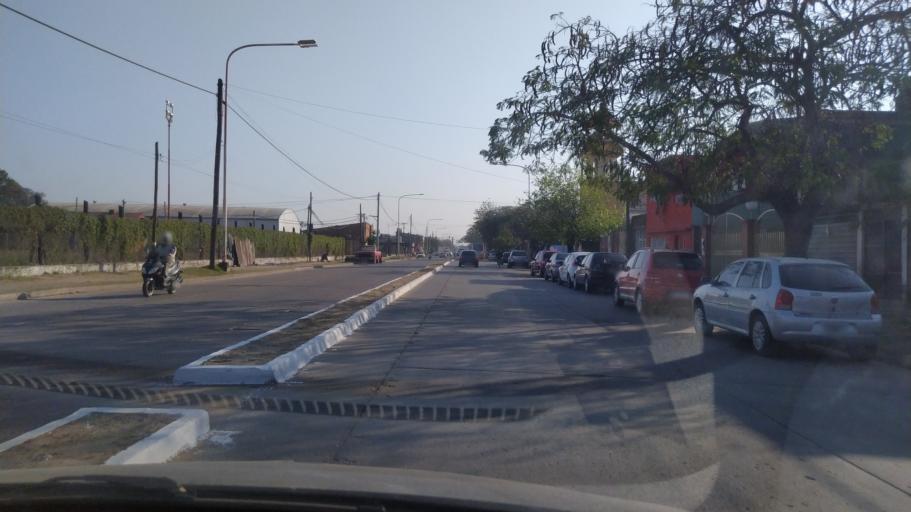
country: AR
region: Corrientes
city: Corrientes
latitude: -27.4850
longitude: -58.8159
